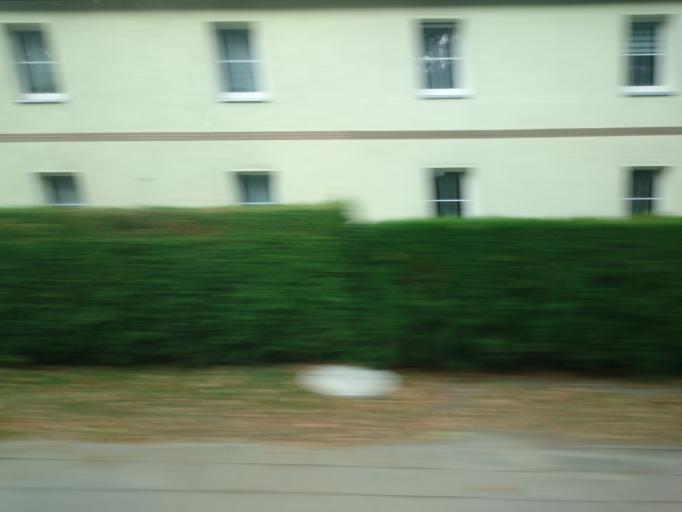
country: DE
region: Mecklenburg-Vorpommern
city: Pasewalk
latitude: 53.4964
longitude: 13.9834
